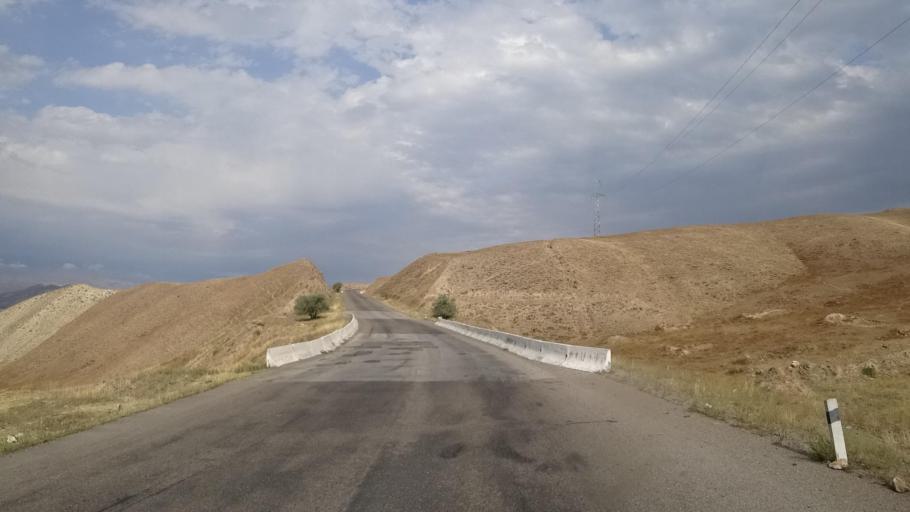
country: KG
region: Jalal-Abad
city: Toktogul
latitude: 41.7804
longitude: 72.9980
